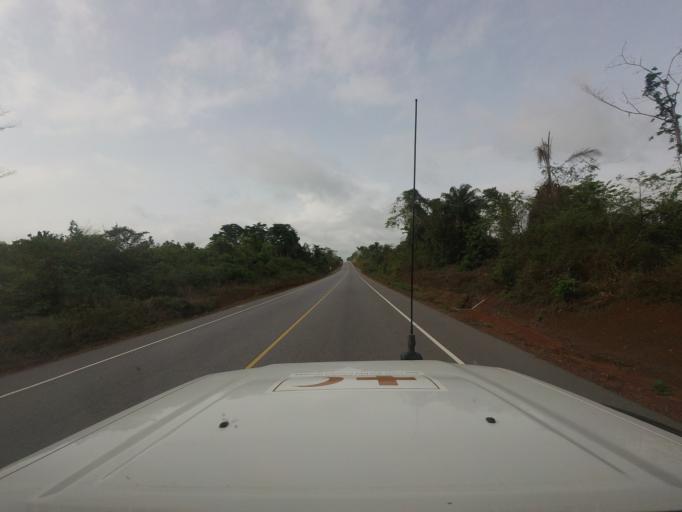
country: LR
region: Bong
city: Gbarnga
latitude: 7.0256
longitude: -9.2728
